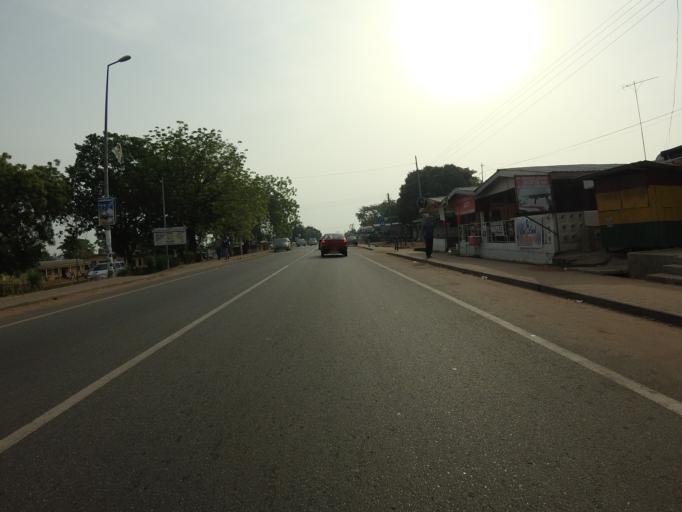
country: GH
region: Volta
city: Ho
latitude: 6.6045
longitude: 0.4765
